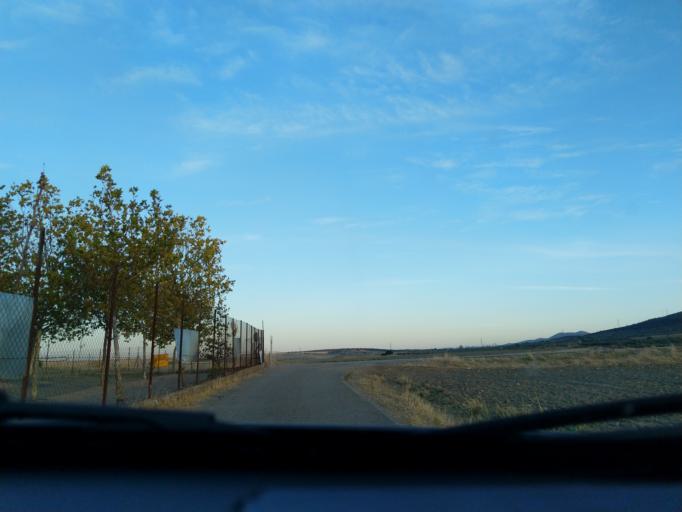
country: ES
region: Extremadura
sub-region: Provincia de Badajoz
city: Casas de Reina
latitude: 38.2012
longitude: -5.9526
